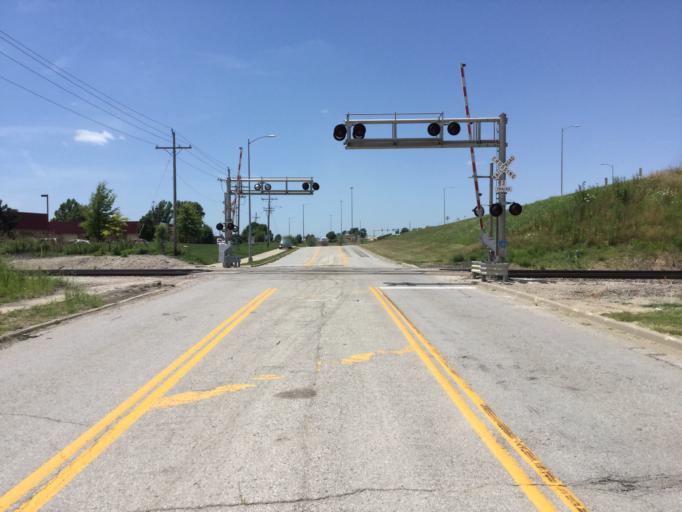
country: US
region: Kansas
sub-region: Johnson County
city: Olathe
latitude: 38.8546
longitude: -94.8087
